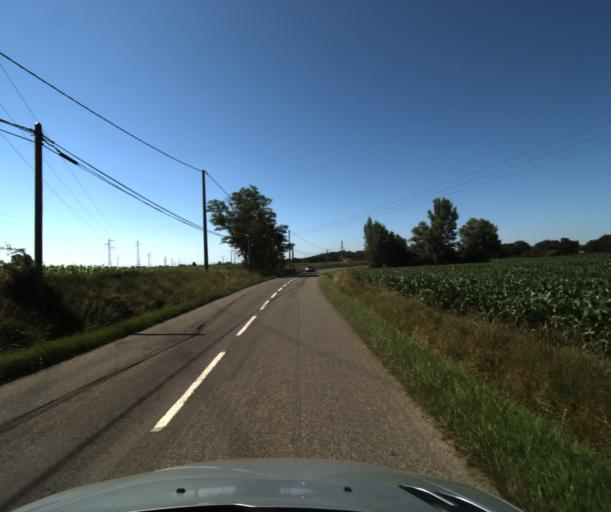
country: FR
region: Midi-Pyrenees
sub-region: Departement de la Haute-Garonne
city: Saubens
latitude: 43.4863
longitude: 1.3518
